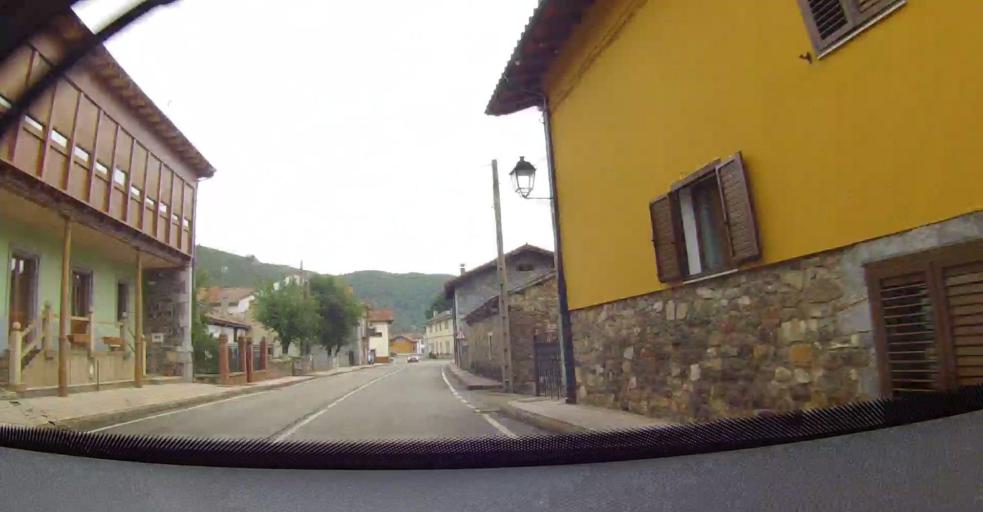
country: ES
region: Castille and Leon
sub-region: Provincia de Leon
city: Acebedo
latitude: 43.0401
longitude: -5.0942
